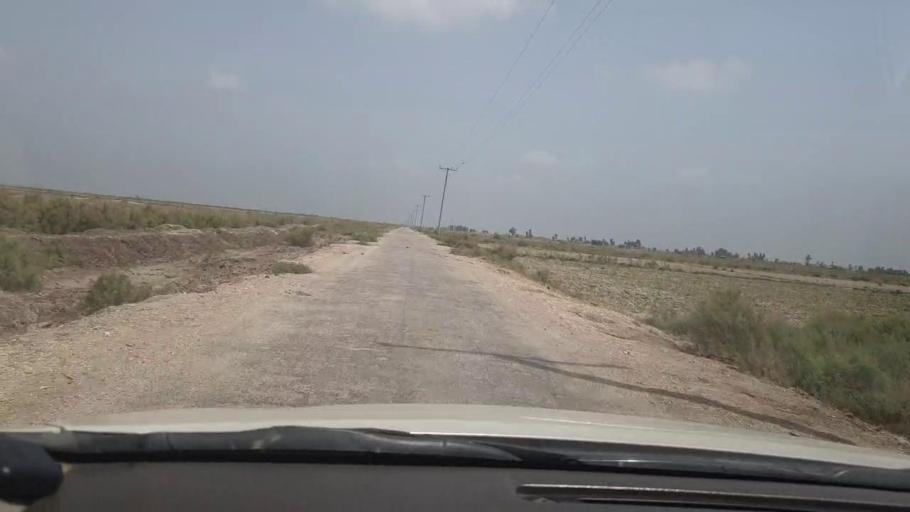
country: PK
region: Sindh
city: Garhi Yasin
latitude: 27.9891
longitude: 68.5016
